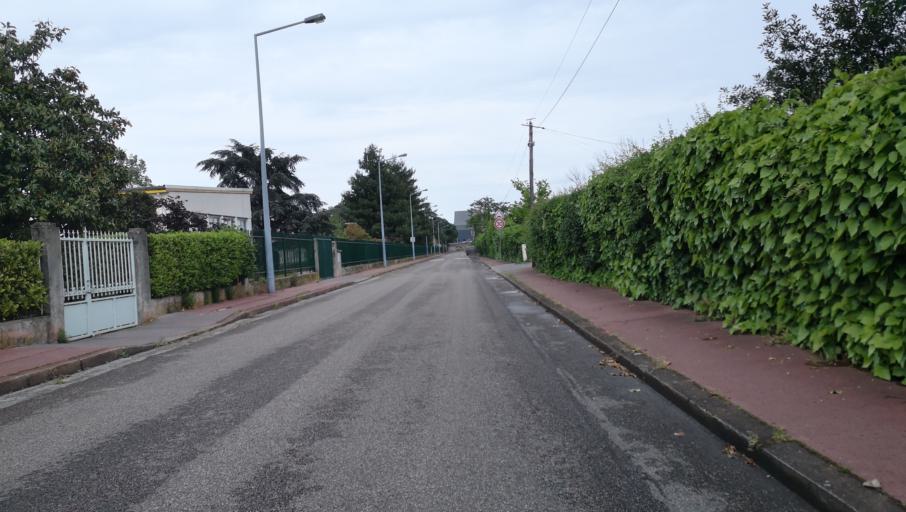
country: FR
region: Rhone-Alpes
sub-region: Departement du Rhone
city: Saint-Fons
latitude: 45.7186
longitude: 4.8651
